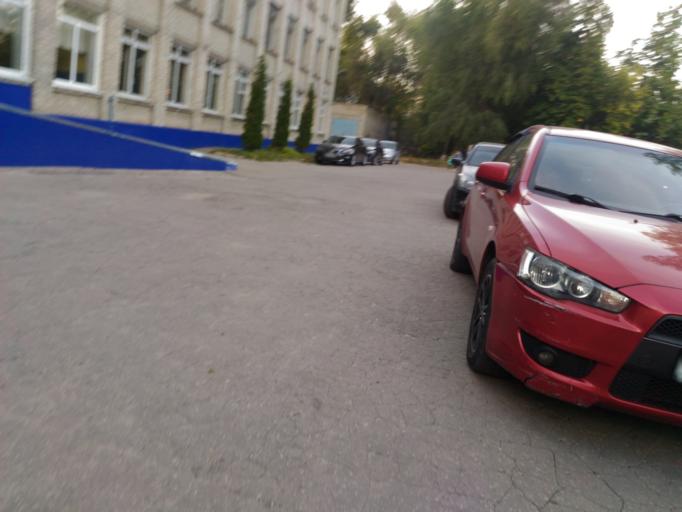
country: RU
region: Ulyanovsk
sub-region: Ulyanovskiy Rayon
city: Ulyanovsk
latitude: 54.2990
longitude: 48.3295
